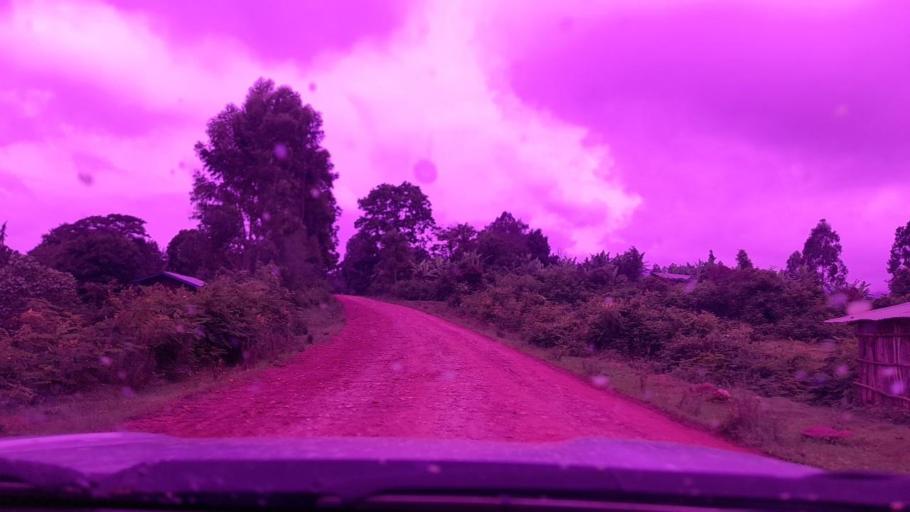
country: ET
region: Southern Nations, Nationalities, and People's Region
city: Bonga
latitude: 7.5511
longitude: 35.8707
